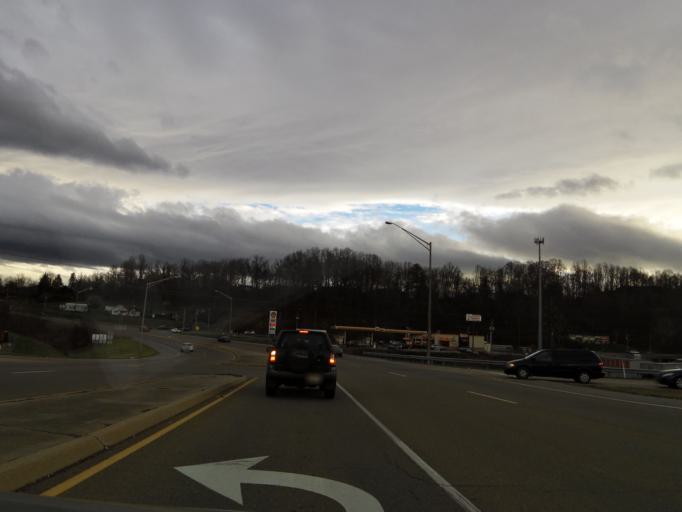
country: US
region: Tennessee
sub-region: Carter County
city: Pine Crest
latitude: 36.3102
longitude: -82.3319
